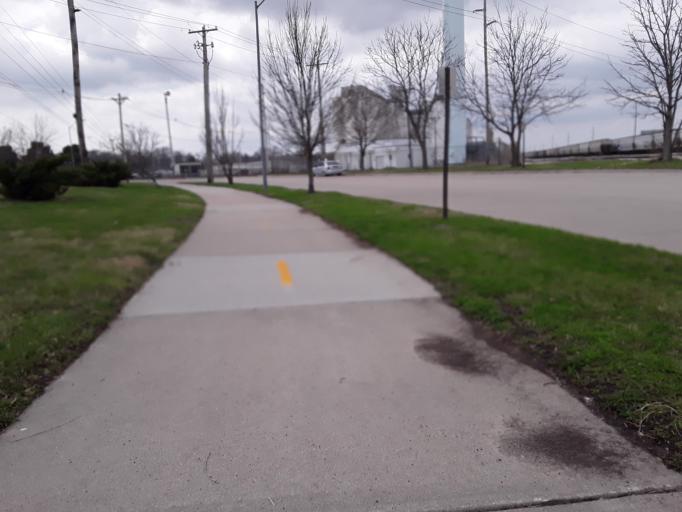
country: US
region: Nebraska
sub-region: Lancaster County
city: Lincoln
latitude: 40.8347
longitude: -96.6828
